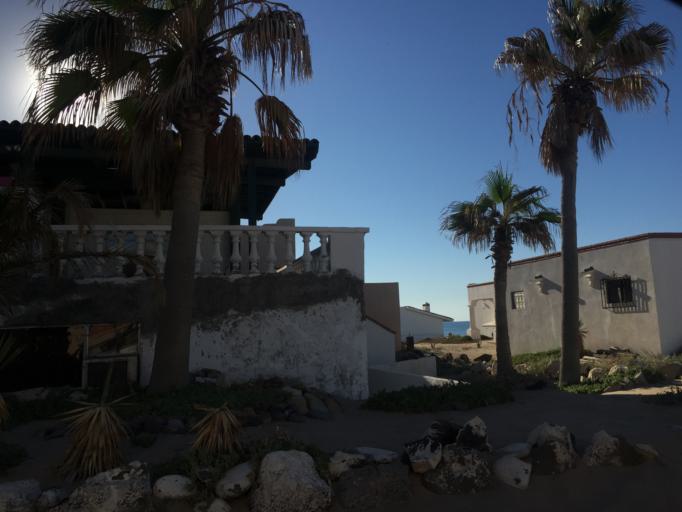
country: MX
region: Sonora
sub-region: Puerto Penasco
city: Puerto Penasco
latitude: 31.2915
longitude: -113.5043
